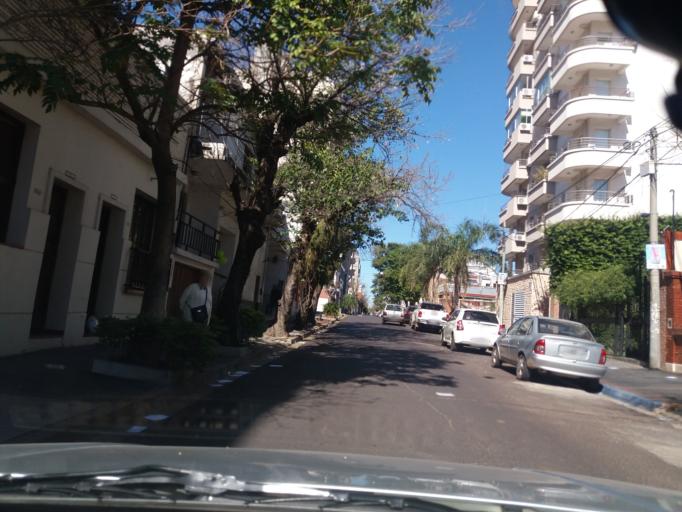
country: AR
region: Corrientes
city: Corrientes
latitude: -27.4677
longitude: -58.8417
